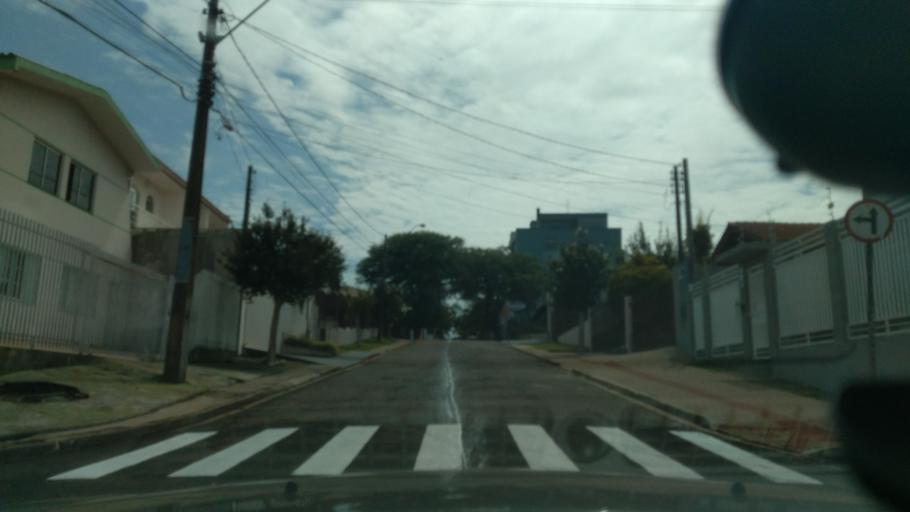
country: BR
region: Parana
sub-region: Guarapuava
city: Guarapuava
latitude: -25.3888
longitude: -51.4687
